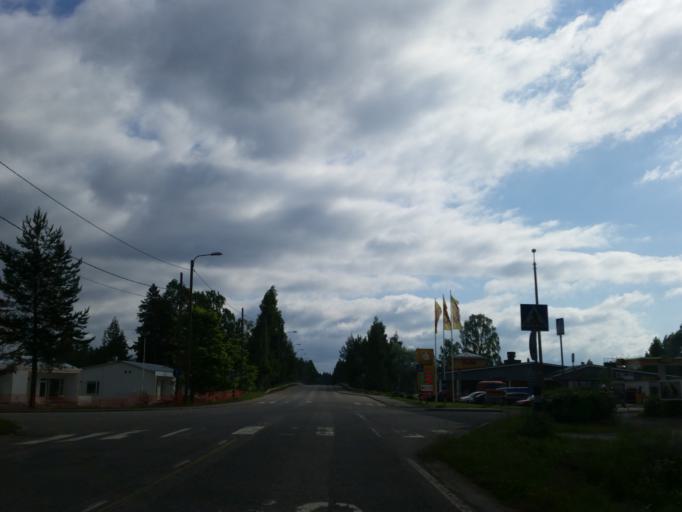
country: FI
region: Northern Savo
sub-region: Sisae-Savo
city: Tervo
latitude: 62.9548
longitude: 26.7522
